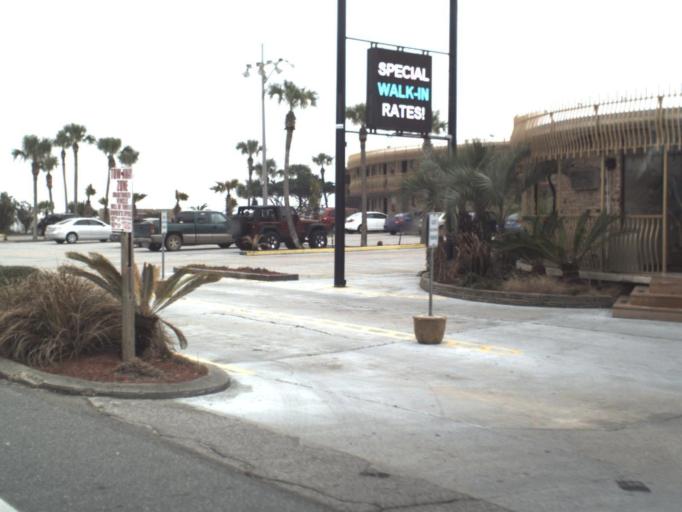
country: US
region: Florida
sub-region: Bay County
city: Panama City Beach
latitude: 30.1929
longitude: -85.8347
